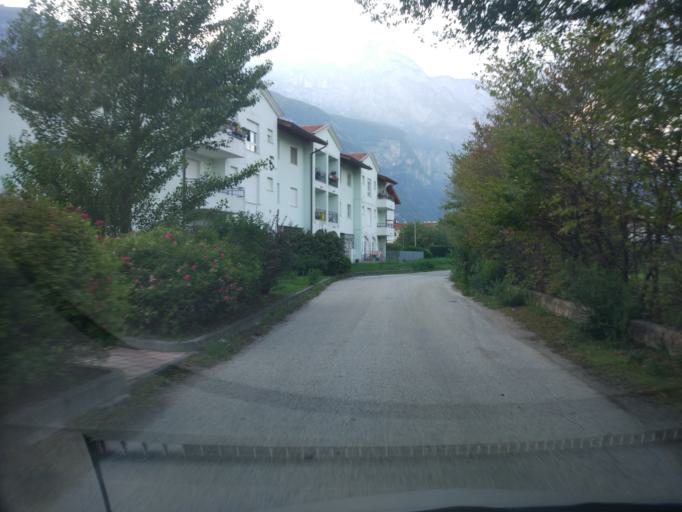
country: IT
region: Trentino-Alto Adige
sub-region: Provincia di Trento
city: Meano
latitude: 46.1204
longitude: 11.0951
